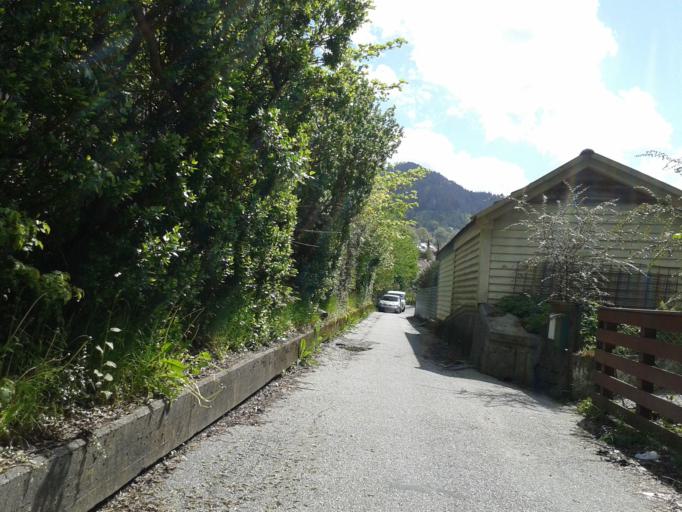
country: NO
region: Hordaland
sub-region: Bergen
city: Bergen
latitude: 60.4143
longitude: 5.3222
